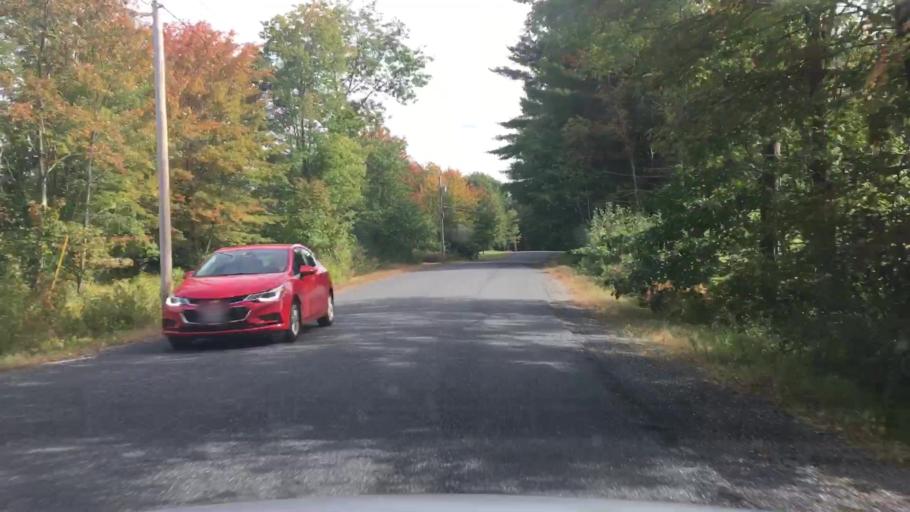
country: US
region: Maine
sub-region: Androscoggin County
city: Lisbon Falls
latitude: 43.9734
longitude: -70.0858
